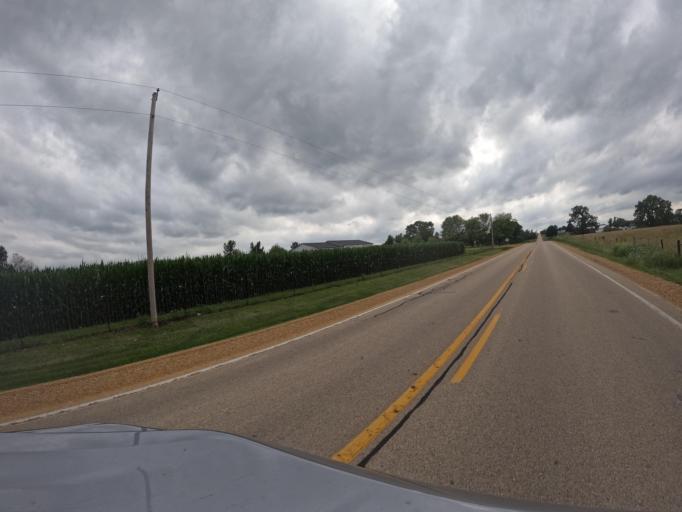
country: US
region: Iowa
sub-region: Clinton County
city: De Witt
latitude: 41.8006
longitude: -90.5124
